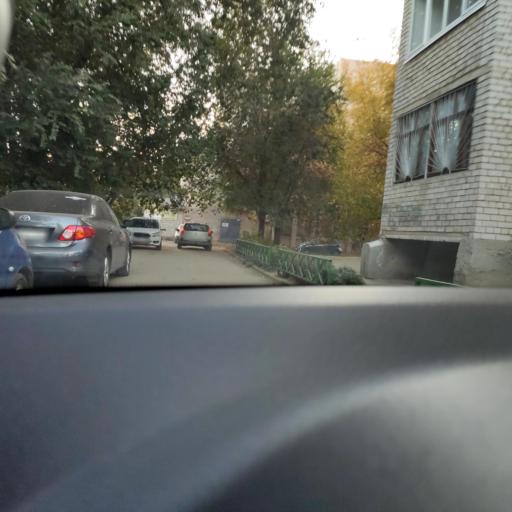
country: RU
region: Samara
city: Samara
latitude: 53.2106
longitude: 50.2563
